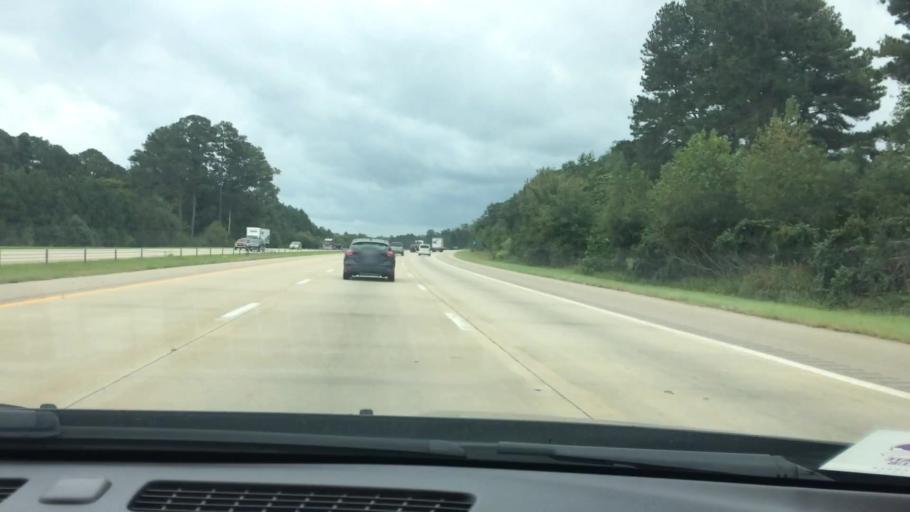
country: US
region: North Carolina
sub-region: Wake County
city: Knightdale
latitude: 35.7670
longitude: -78.4863
